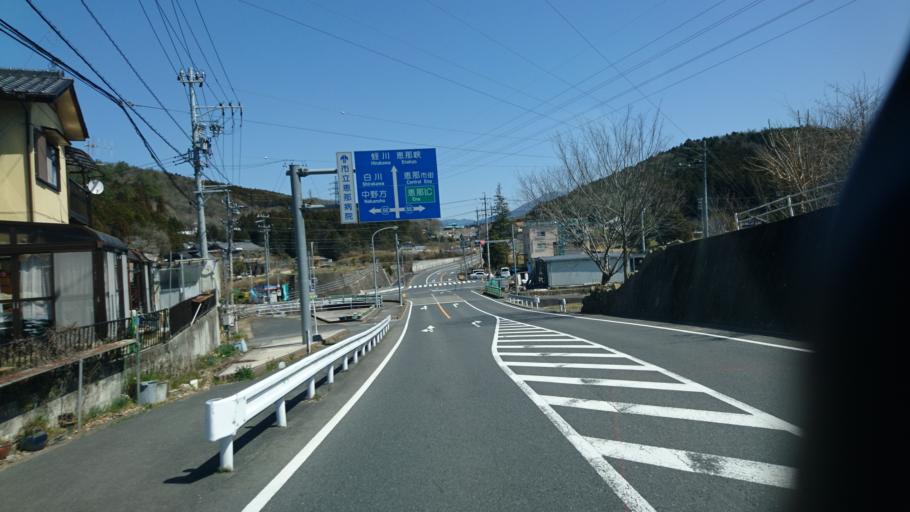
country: JP
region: Gifu
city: Nakatsugawa
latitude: 35.4643
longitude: 137.3845
